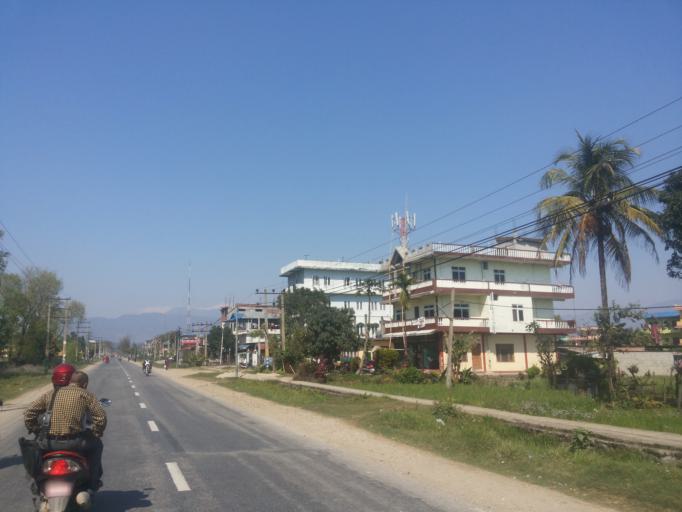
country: NP
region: Central Region
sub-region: Narayani Zone
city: Bharatpur
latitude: 27.6818
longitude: 84.4394
